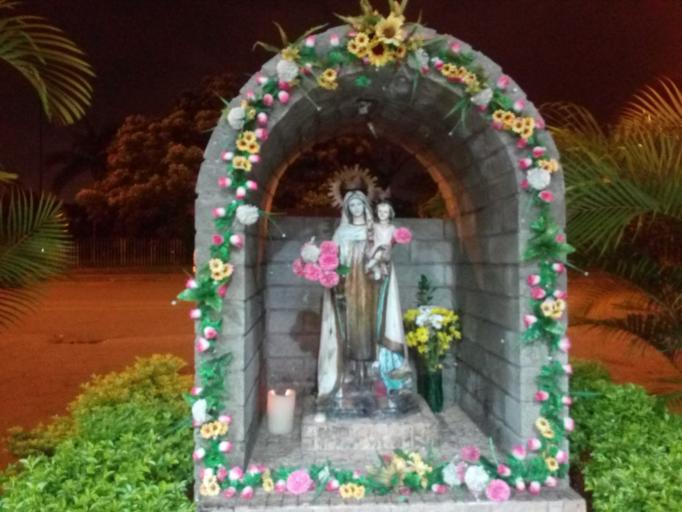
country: CO
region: Antioquia
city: Itagui
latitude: 6.1887
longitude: -75.5884
